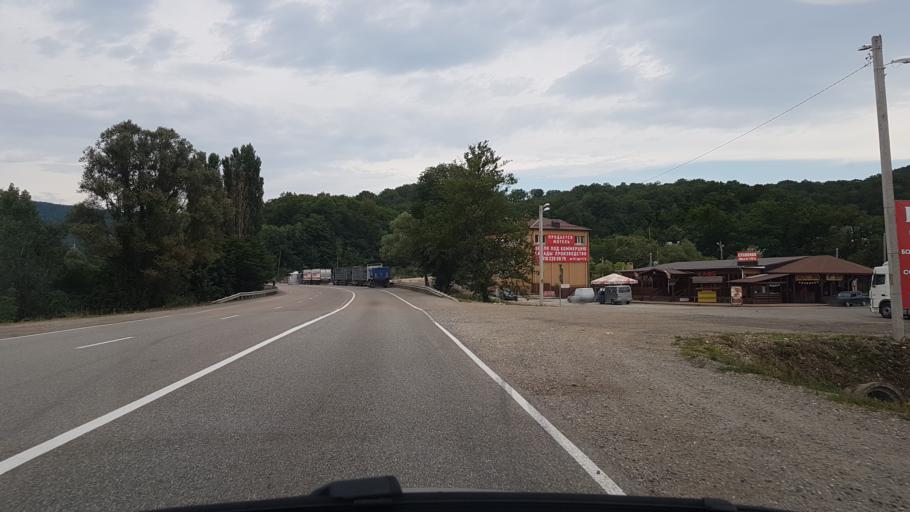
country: RU
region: Krasnodarskiy
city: Lermontovo
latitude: 44.4401
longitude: 38.7858
